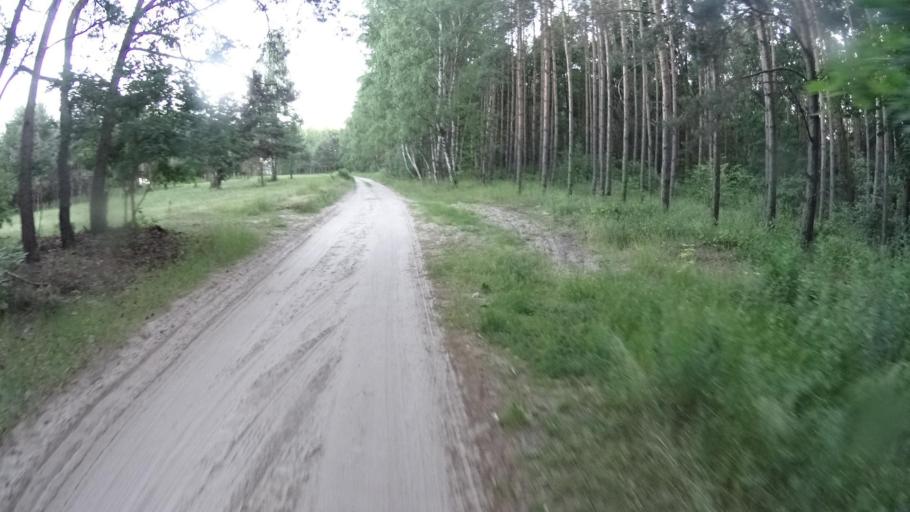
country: PL
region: Masovian Voivodeship
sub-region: Powiat warszawski zachodni
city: Jozefow
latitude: 52.2711
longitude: 20.6955
